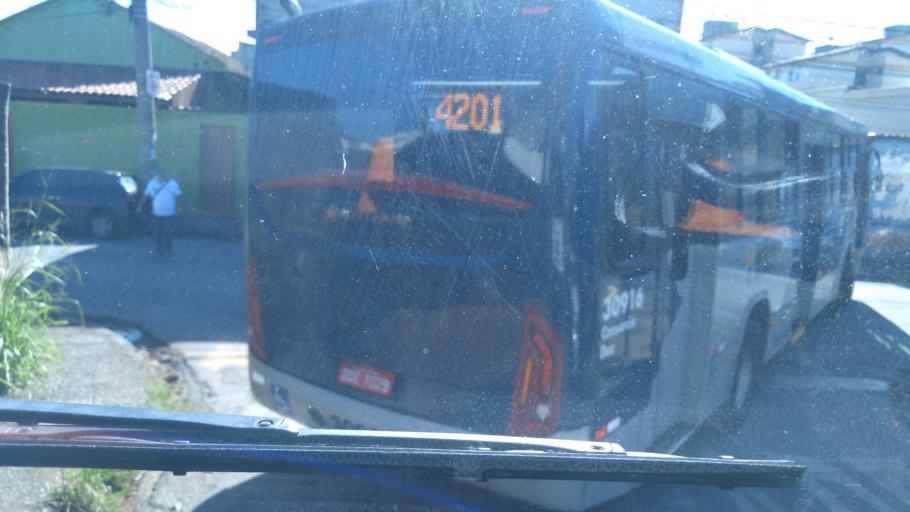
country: BR
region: Minas Gerais
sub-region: Belo Horizonte
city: Belo Horizonte
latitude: -19.9049
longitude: -43.9564
